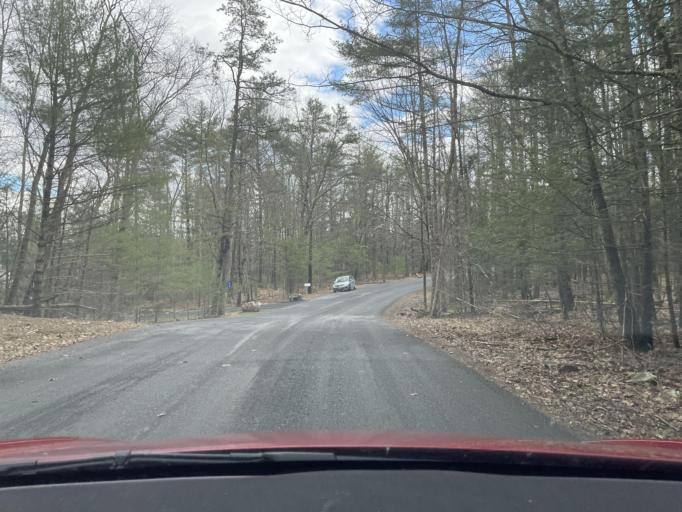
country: US
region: New York
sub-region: Ulster County
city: Zena
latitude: 42.0342
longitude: -74.0563
